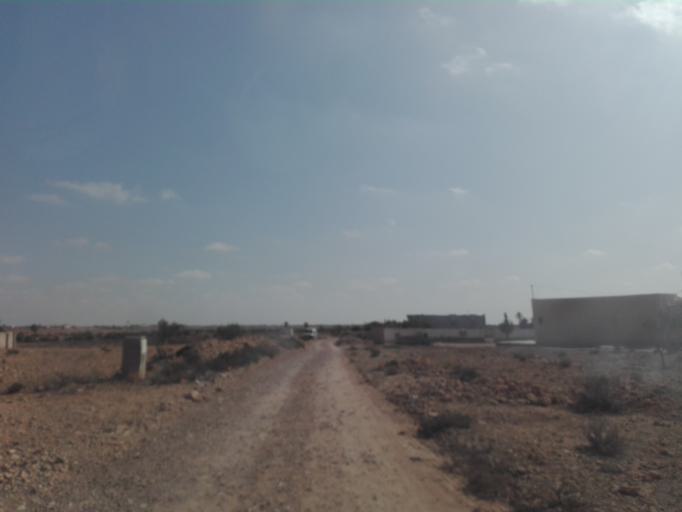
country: TN
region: Madanin
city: Medenine
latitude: 33.4335
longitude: 10.4193
